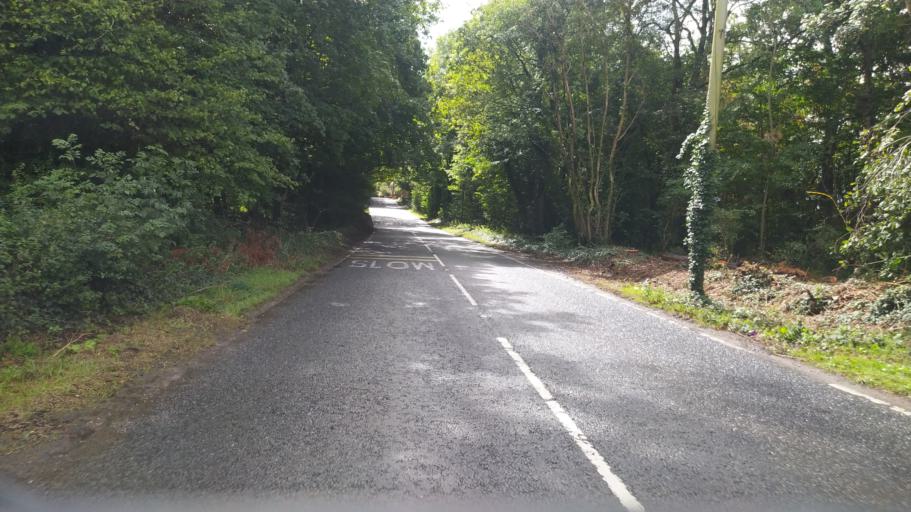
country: GB
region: England
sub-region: Dorset
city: Sherborne
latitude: 50.9211
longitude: -2.5071
